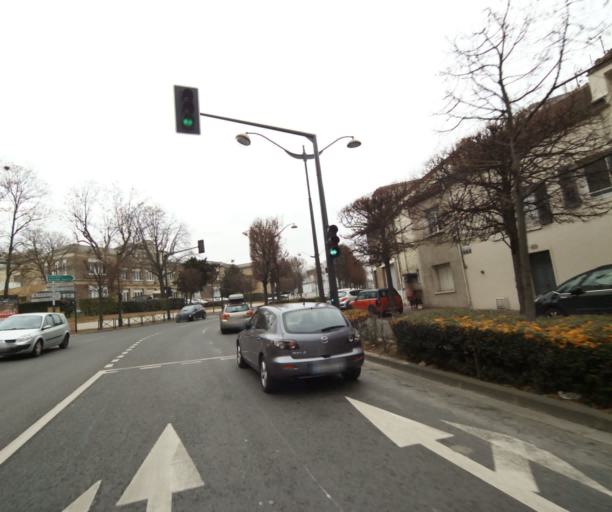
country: FR
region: Ile-de-France
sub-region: Departement des Hauts-de-Seine
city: Rueil-Malmaison
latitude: 48.8772
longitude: 2.1867
